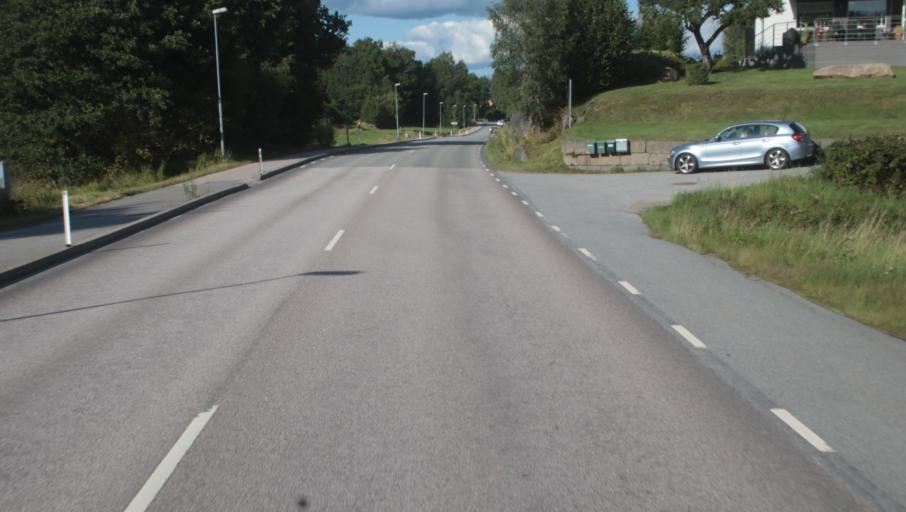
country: SE
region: Blekinge
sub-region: Karlshamns Kommun
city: Karlshamn
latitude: 56.1749
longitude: 14.9022
